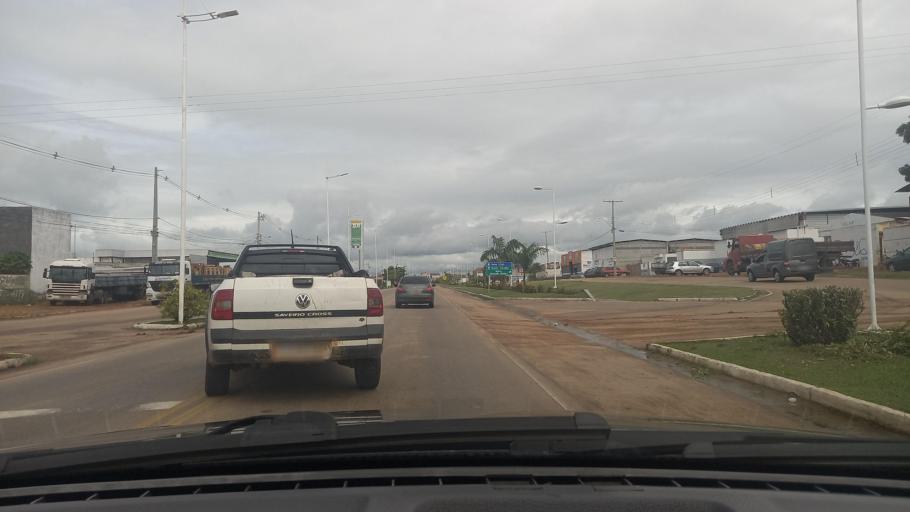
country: BR
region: Bahia
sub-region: Paulo Afonso
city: Paulo Afonso
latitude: -9.4380
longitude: -38.2251
